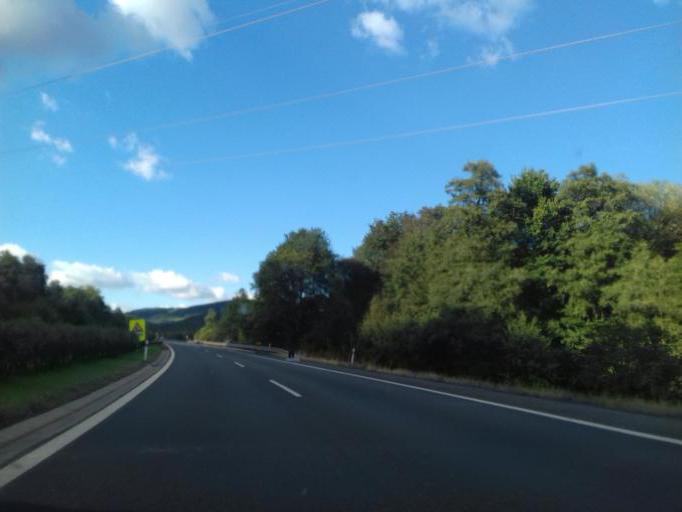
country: CZ
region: Liberecky
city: Hodkovice nad Mohelkou
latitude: 50.6594
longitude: 15.0983
